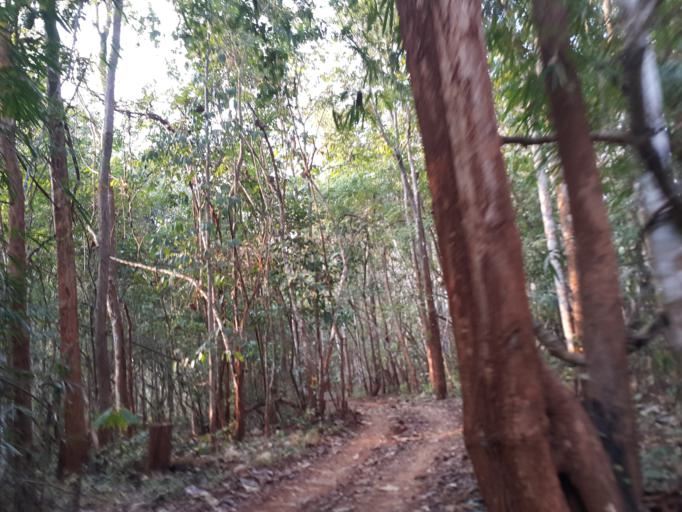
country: TH
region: Lamphun
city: Li
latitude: 17.6167
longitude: 98.8992
